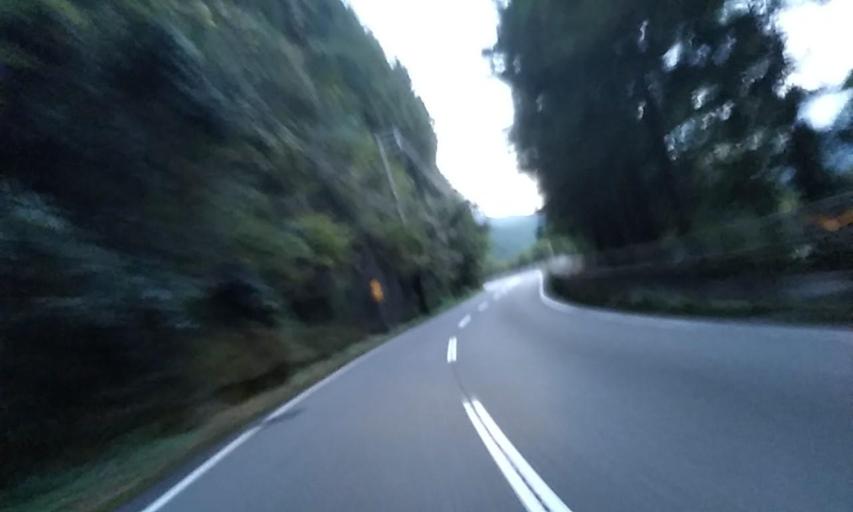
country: JP
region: Wakayama
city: Shingu
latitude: 33.7311
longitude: 135.9460
